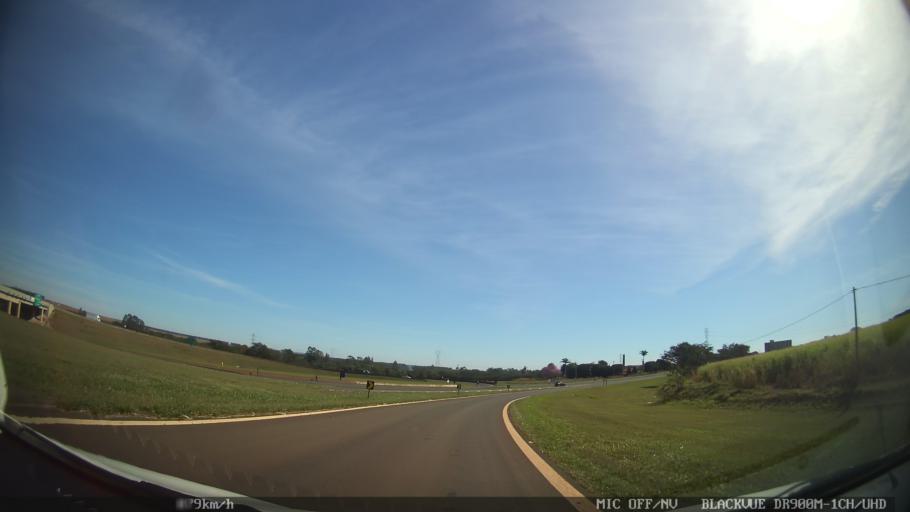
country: BR
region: Sao Paulo
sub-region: Porto Ferreira
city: Porto Ferreira
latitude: -21.8346
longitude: -47.4944
